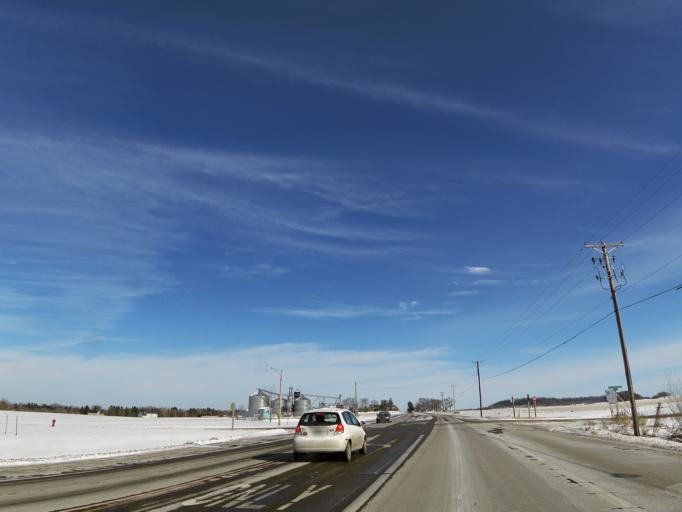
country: US
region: Wisconsin
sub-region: Pierce County
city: Prescott
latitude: 44.7639
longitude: -92.7893
